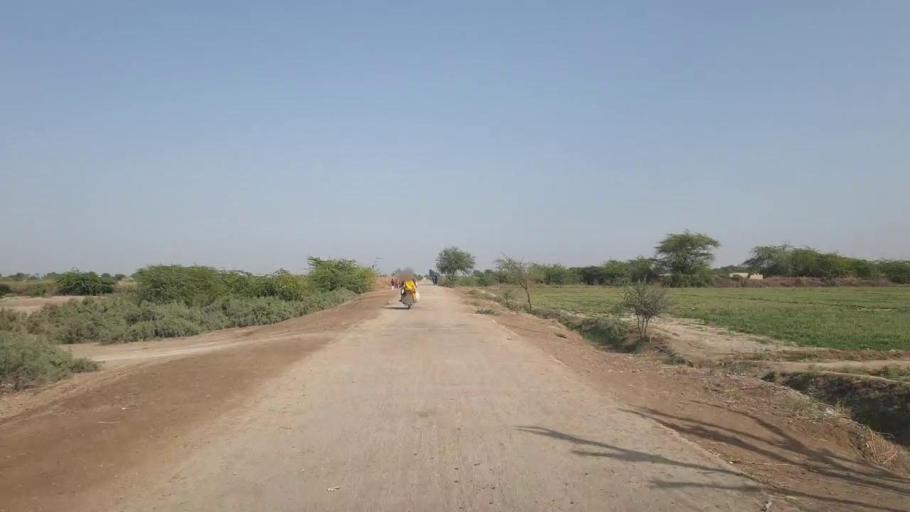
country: PK
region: Sindh
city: Dhoro Naro
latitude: 25.4420
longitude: 69.5368
